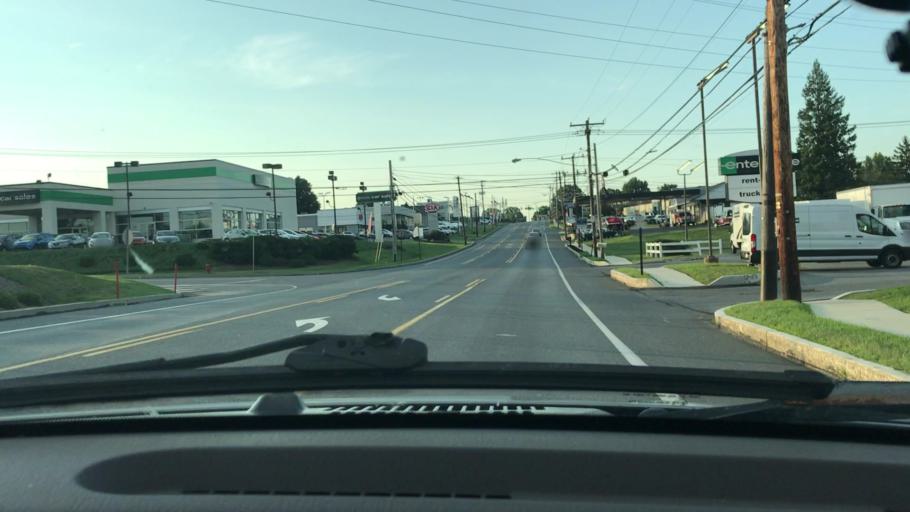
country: US
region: Pennsylvania
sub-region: Lancaster County
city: East Petersburg
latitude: 40.0865
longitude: -76.3455
